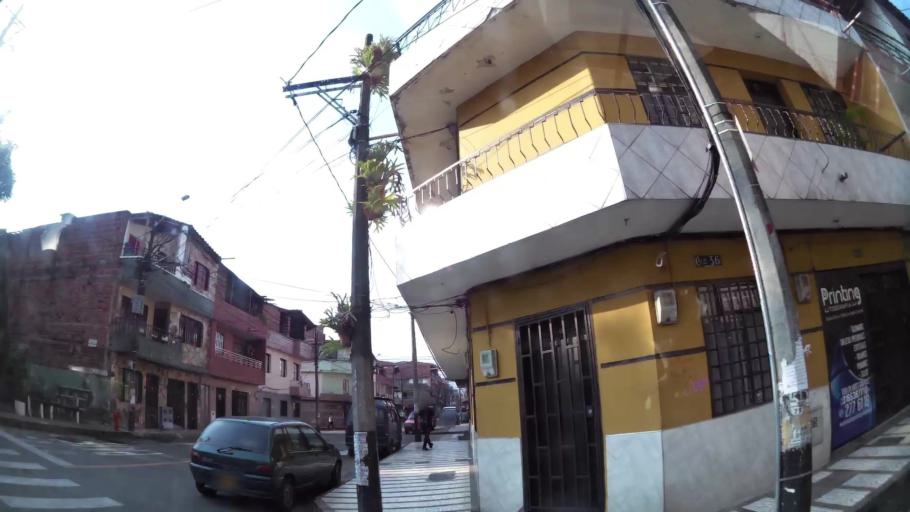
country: CO
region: Antioquia
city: Sabaneta
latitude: 6.1663
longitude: -75.6190
